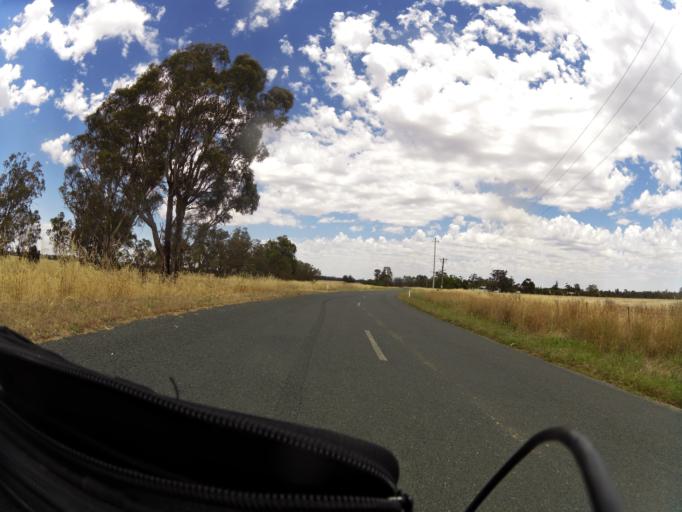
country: AU
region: Victoria
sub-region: Greater Shepparton
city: Shepparton
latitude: -36.6673
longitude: 145.1987
